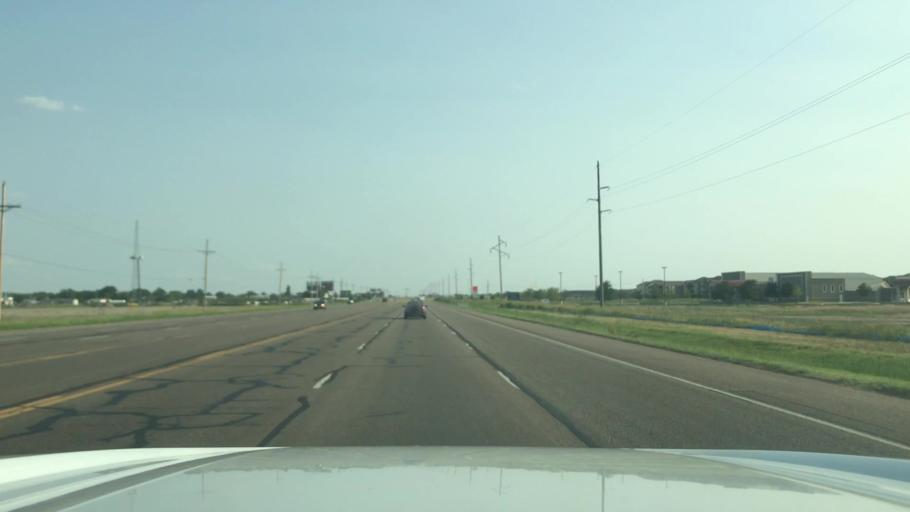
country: US
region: Texas
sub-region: Potter County
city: Amarillo
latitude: 35.1360
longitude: -101.9382
